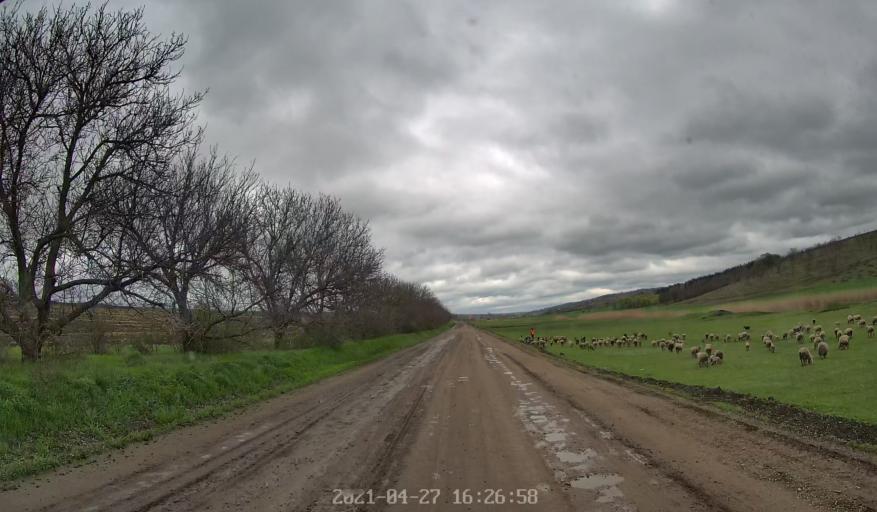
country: MD
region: Chisinau
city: Singera
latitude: 46.9773
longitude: 29.0304
